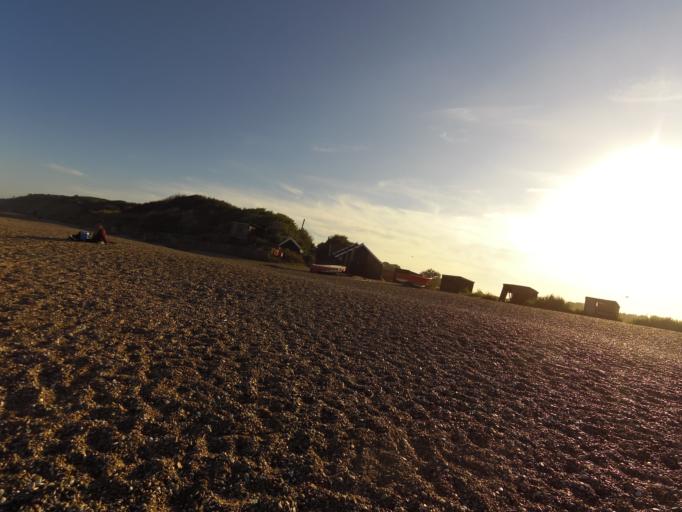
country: GB
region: England
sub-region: Suffolk
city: Southwold
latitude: 52.2787
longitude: 1.6339
